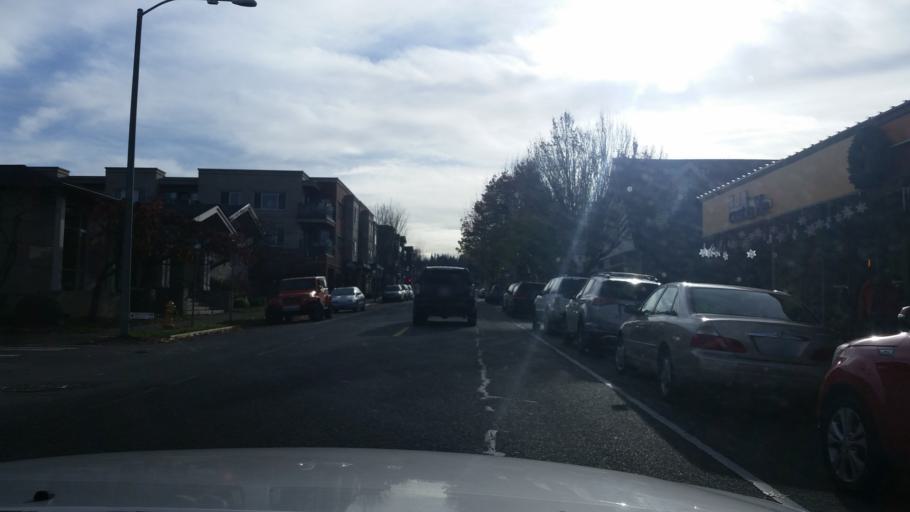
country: US
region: Washington
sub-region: Snohomish County
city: Edmonds
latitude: 47.8082
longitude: -122.3776
